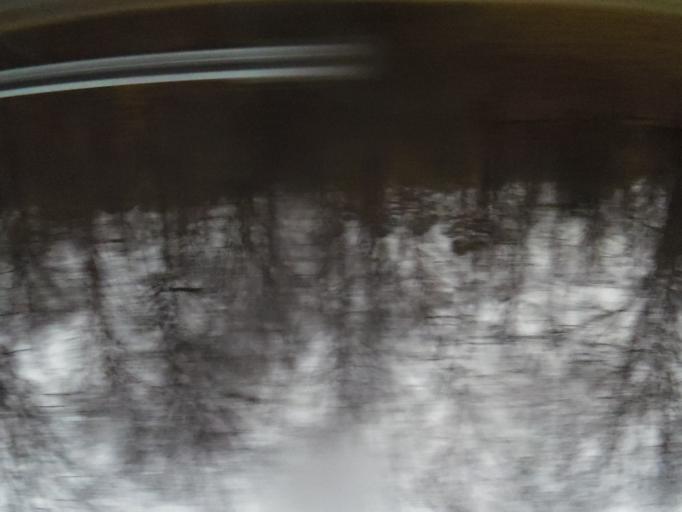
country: US
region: Alabama
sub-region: Cullman County
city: Cullman
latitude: 34.1956
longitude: -86.8787
